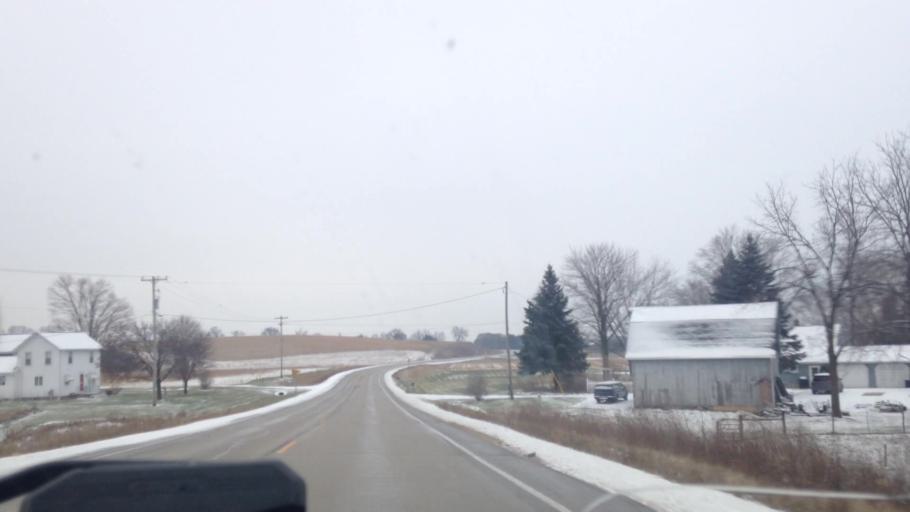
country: US
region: Wisconsin
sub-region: Jefferson County
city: Ixonia
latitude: 43.2390
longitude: -88.5183
